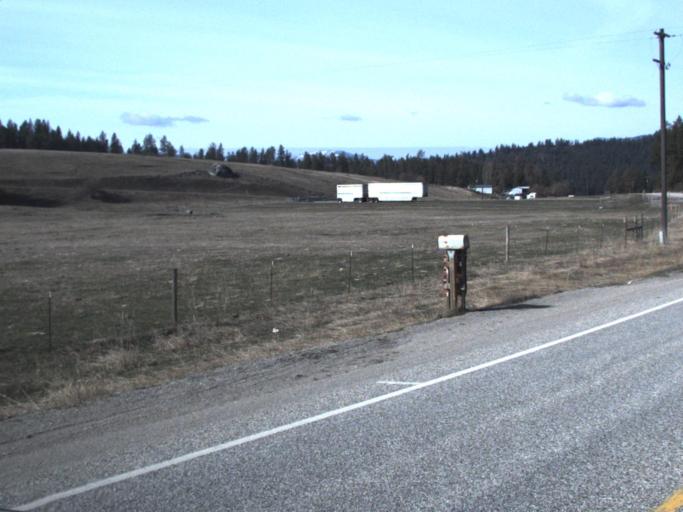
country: US
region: Washington
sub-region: Stevens County
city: Colville
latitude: 48.5161
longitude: -117.7924
